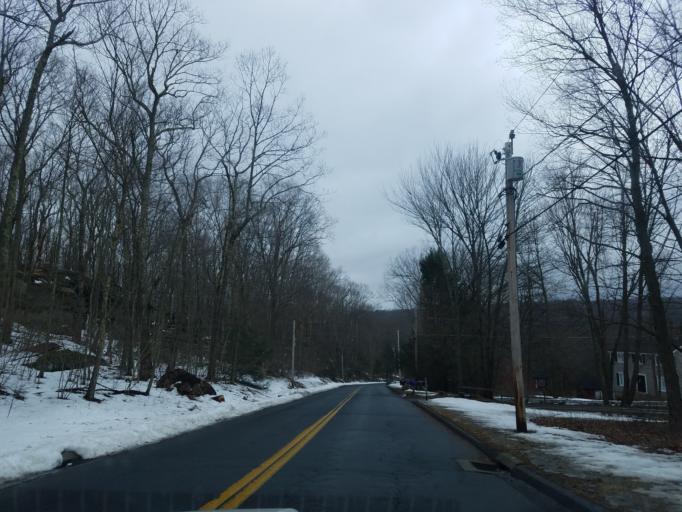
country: US
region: Connecticut
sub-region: Hartford County
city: Glastonbury Center
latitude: 41.6662
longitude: -72.5636
